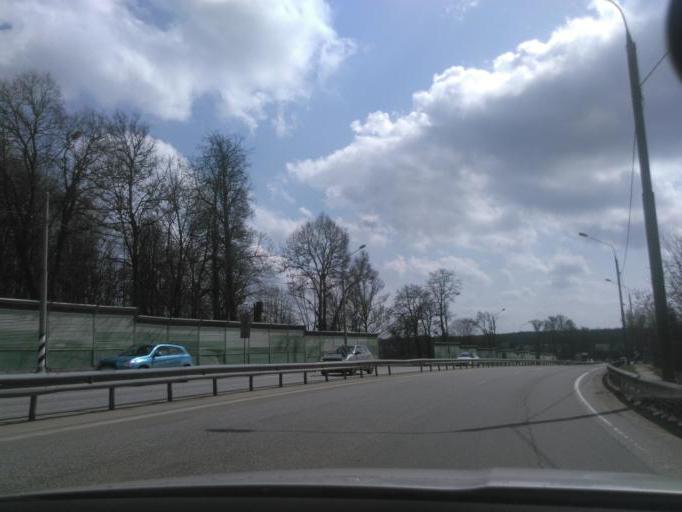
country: RU
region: Moskovskaya
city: Chashnikovo
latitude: 56.0352
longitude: 37.1637
